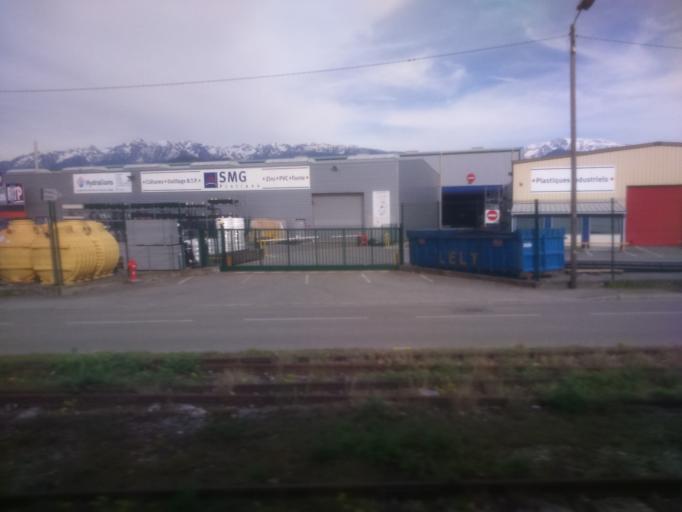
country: FR
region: Rhone-Alpes
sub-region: Departement de l'Isere
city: Grenoble
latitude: 45.1551
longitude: 5.7089
